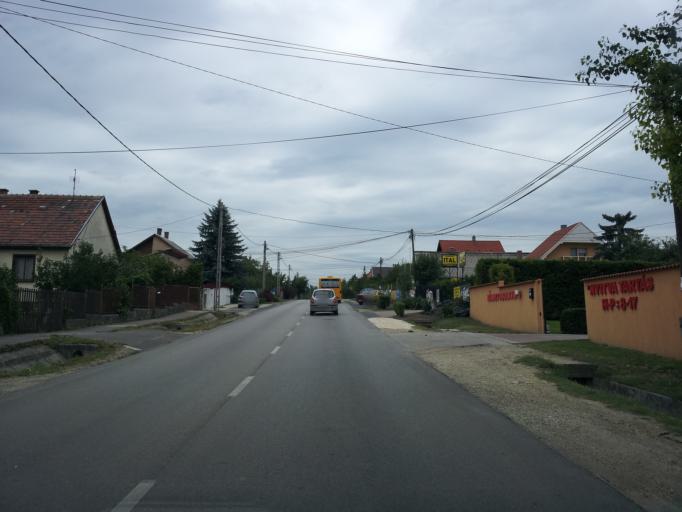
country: HU
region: Pest
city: Erd
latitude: 47.3936
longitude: 18.8969
